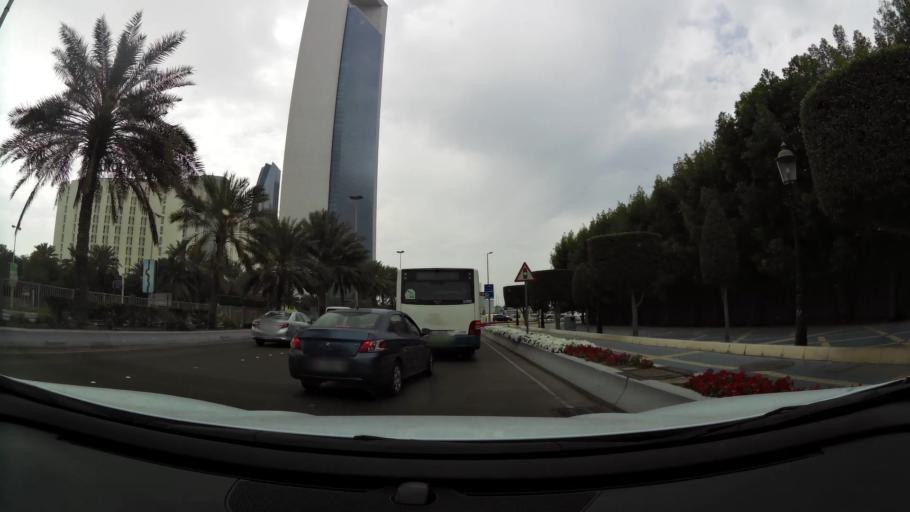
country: AE
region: Abu Dhabi
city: Abu Dhabi
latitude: 24.4646
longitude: 54.3265
